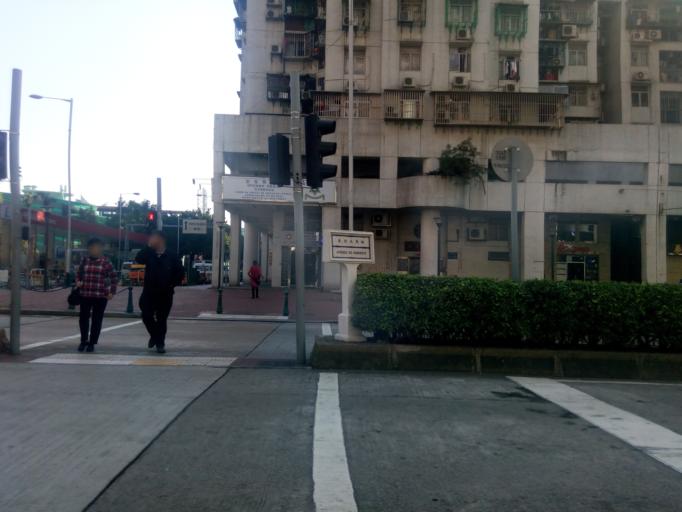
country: MO
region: Macau
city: Macau
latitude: 22.2081
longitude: 113.5567
